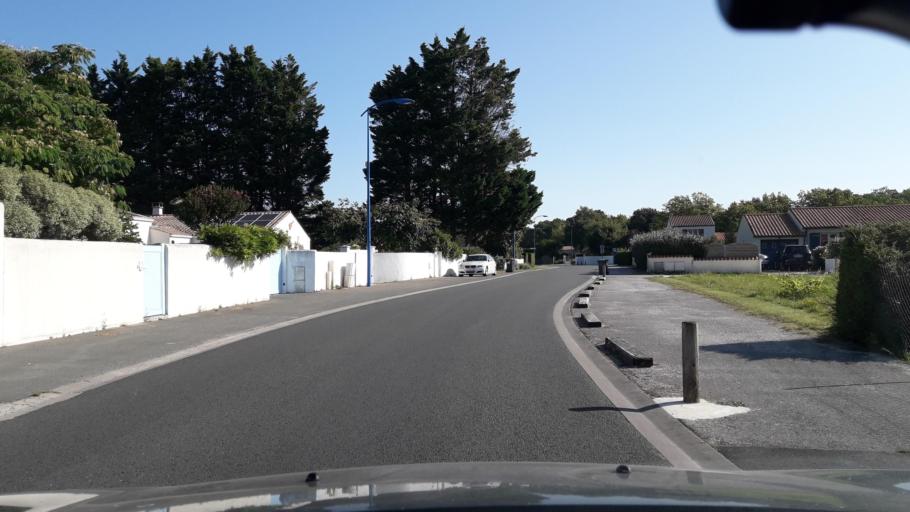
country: FR
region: Poitou-Charentes
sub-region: Departement de la Charente-Maritime
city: Etaules
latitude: 45.7232
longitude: -1.1031
